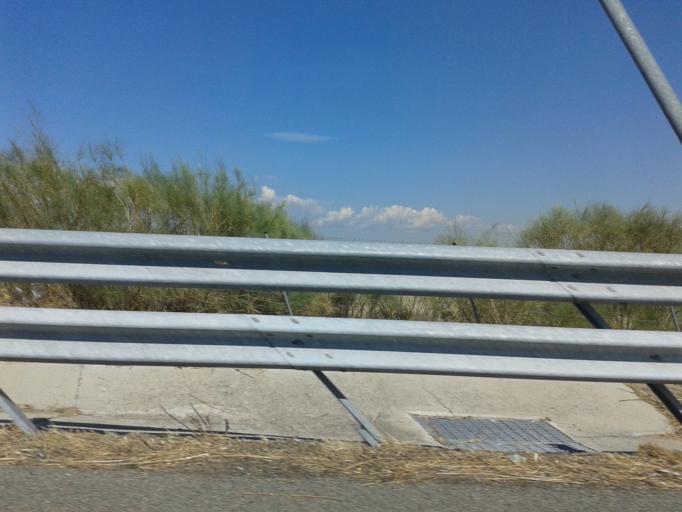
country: ES
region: Madrid
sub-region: Provincia de Madrid
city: Barajas de Madrid
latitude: 40.4801
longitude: -3.5980
